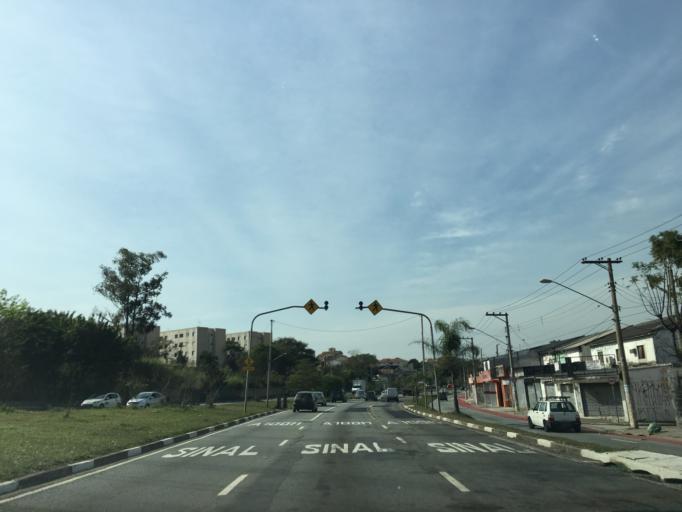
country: BR
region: Sao Paulo
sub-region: Osasco
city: Osasco
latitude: -23.5646
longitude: -46.7544
